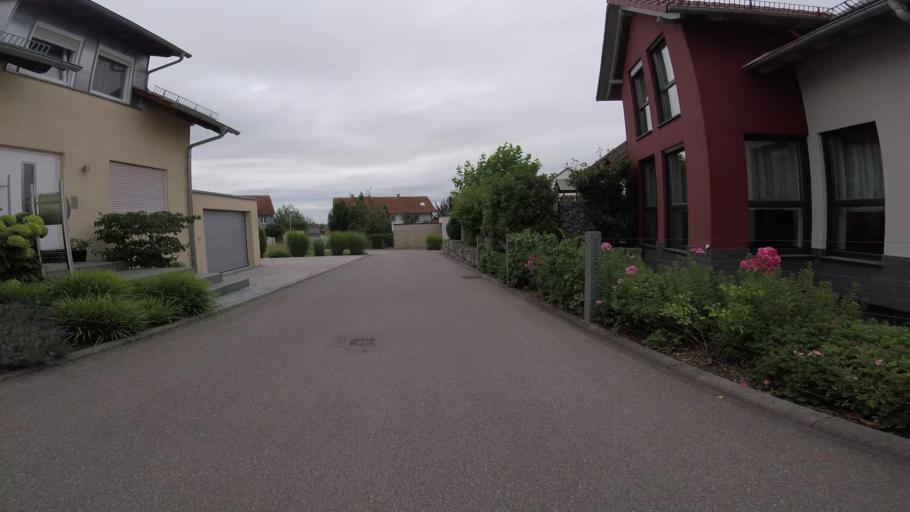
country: DE
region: Baden-Wuerttemberg
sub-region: Regierungsbezirk Stuttgart
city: Aspach
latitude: 48.9651
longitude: 9.4082
